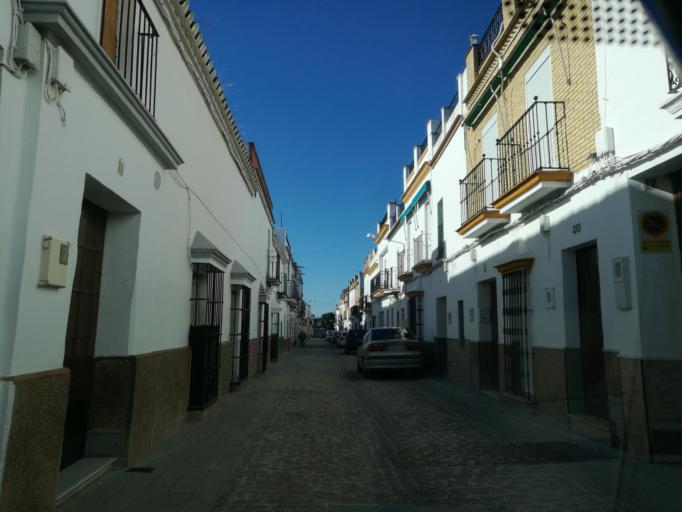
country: ES
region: Andalusia
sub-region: Provincia de Sevilla
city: La Campana
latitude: 37.5701
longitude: -5.4276
